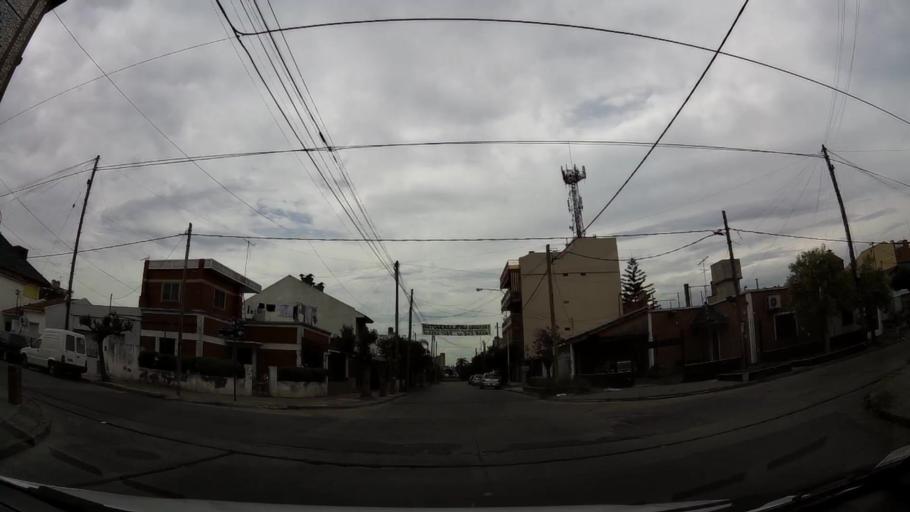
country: AR
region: Buenos Aires F.D.
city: Villa Lugano
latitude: -34.6699
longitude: -58.5104
